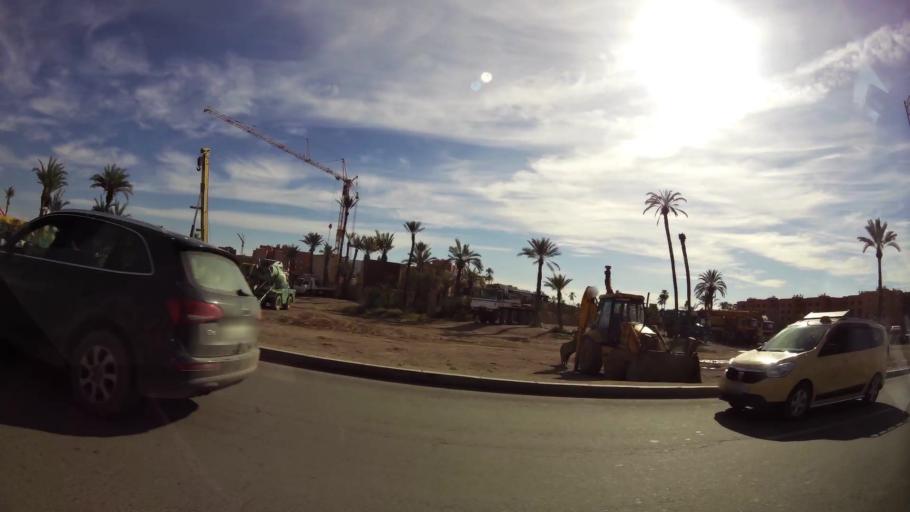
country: MA
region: Marrakech-Tensift-Al Haouz
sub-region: Marrakech
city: Marrakesh
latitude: 31.6585
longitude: -8.0238
